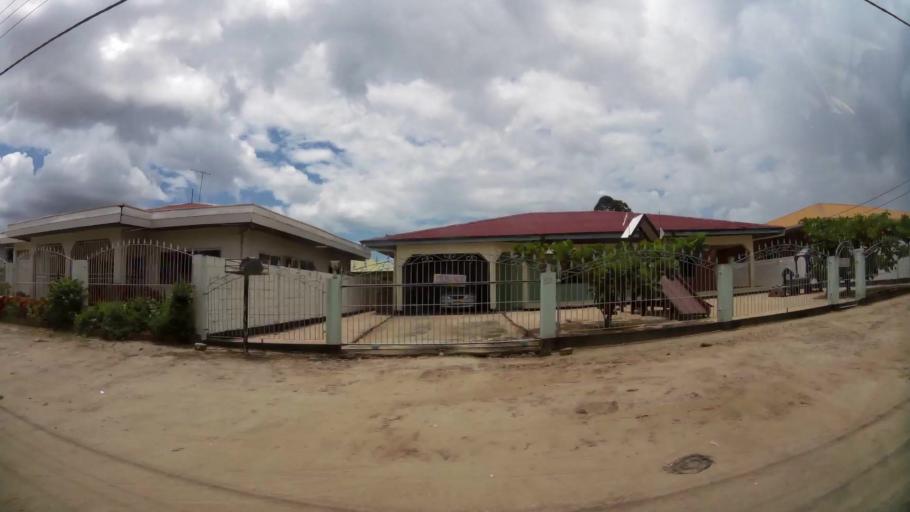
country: SR
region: Paramaribo
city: Paramaribo
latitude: 5.8549
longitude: -55.1387
